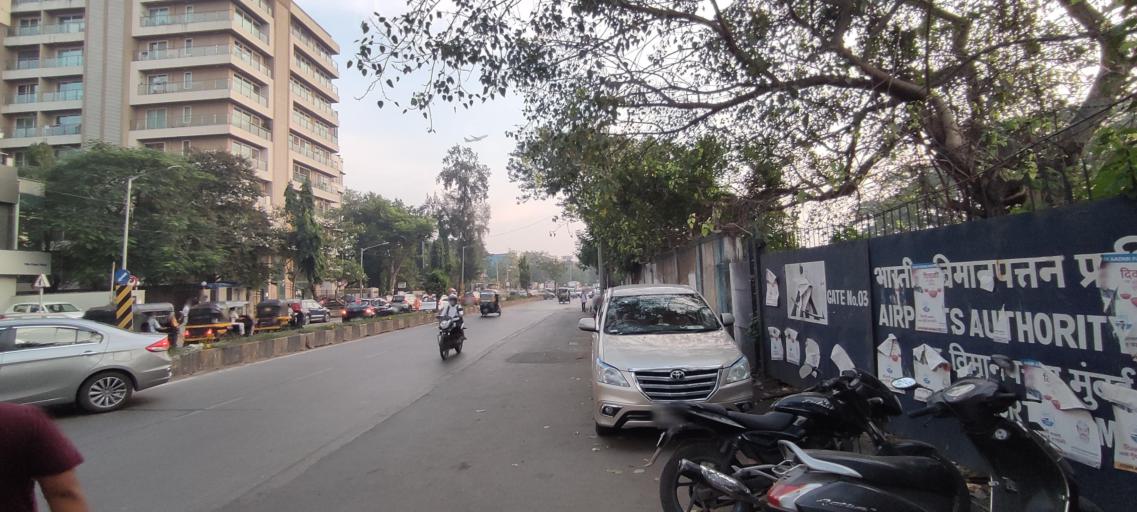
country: IN
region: Maharashtra
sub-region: Mumbai Suburban
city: Mumbai
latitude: 19.0952
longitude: 72.8395
